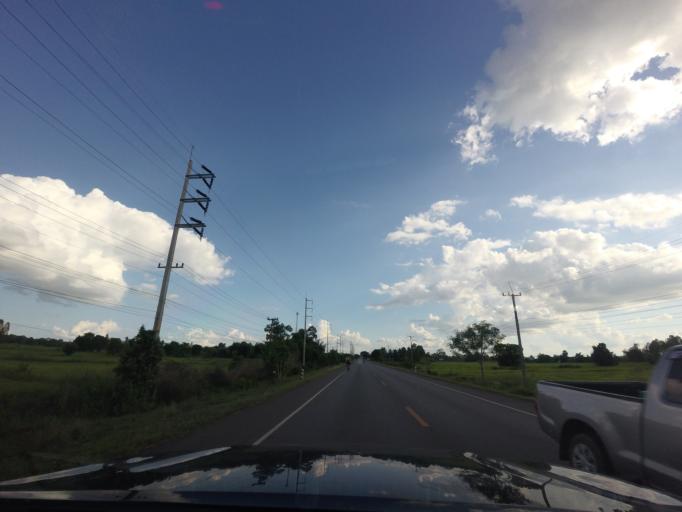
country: TH
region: Changwat Udon Thani
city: Thung Fon
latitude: 17.5113
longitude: 103.2033
